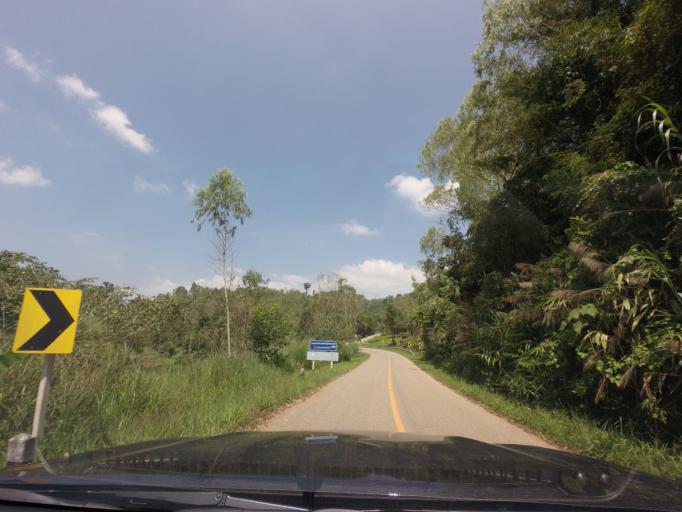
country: TH
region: Loei
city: Na Haeo
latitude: 17.5982
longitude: 100.9022
